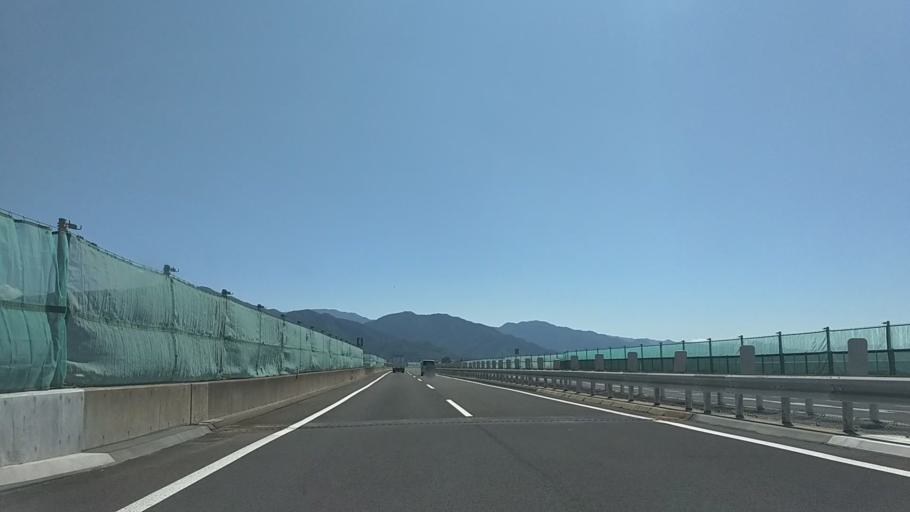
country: JP
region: Nagano
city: Suzaka
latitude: 36.6804
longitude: 138.2905
